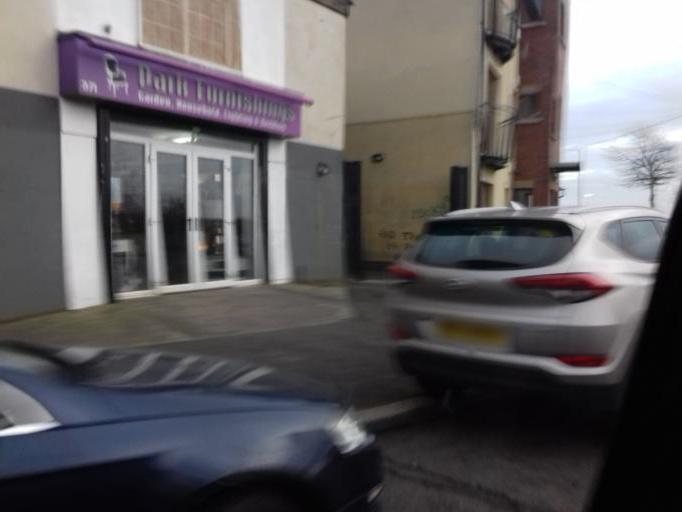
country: GB
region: Northern Ireland
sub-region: City of Belfast
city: Belfast
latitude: 54.6177
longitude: -5.9542
